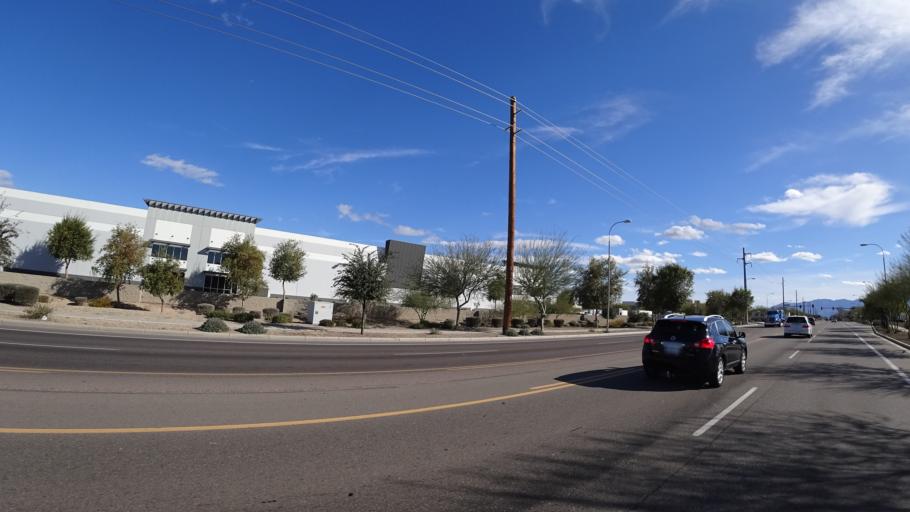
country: US
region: Arizona
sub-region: Maricopa County
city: Tolleson
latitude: 33.4321
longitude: -112.2209
